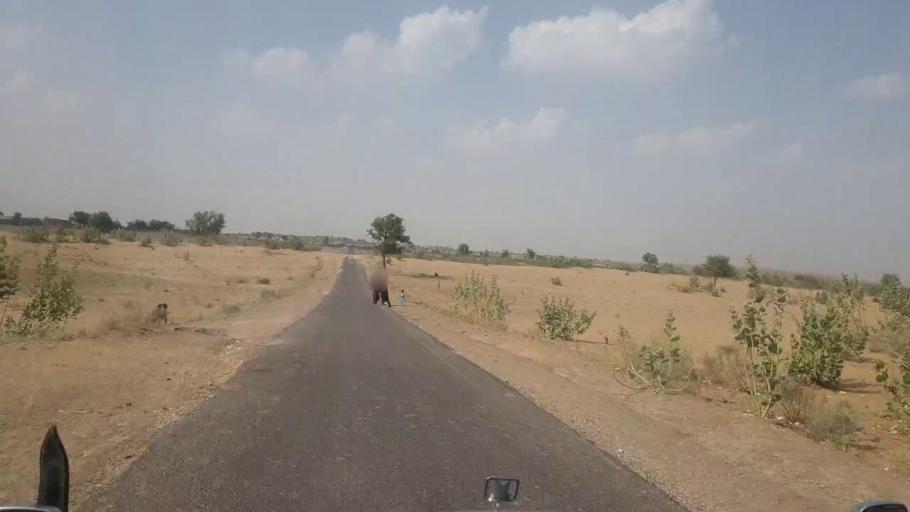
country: PK
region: Sindh
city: Islamkot
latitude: 25.2218
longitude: 70.2884
